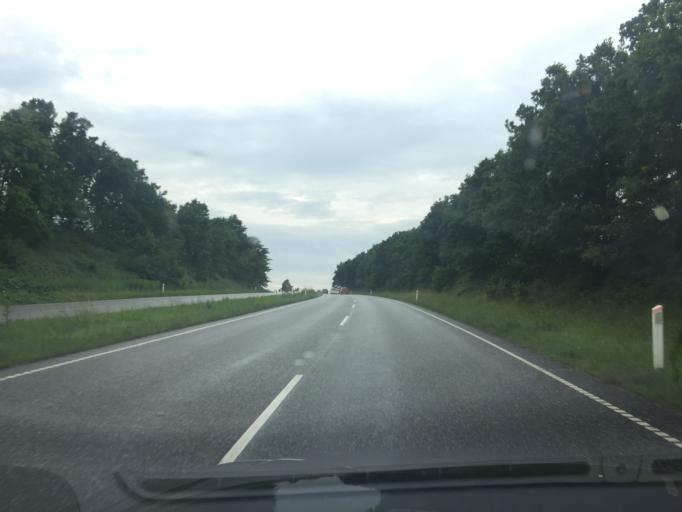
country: DK
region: Capital Region
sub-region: Egedal Kommune
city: Vekso
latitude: 55.7544
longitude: 12.2483
